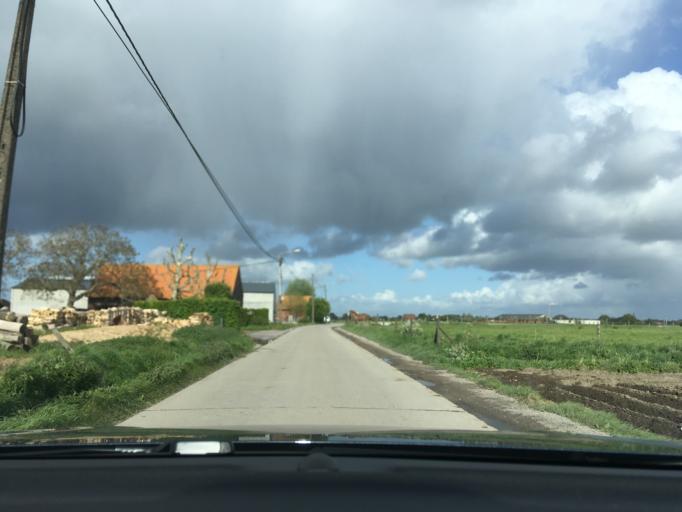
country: BE
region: Flanders
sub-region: Provincie West-Vlaanderen
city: Hooglede
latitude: 51.0003
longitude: 3.0657
